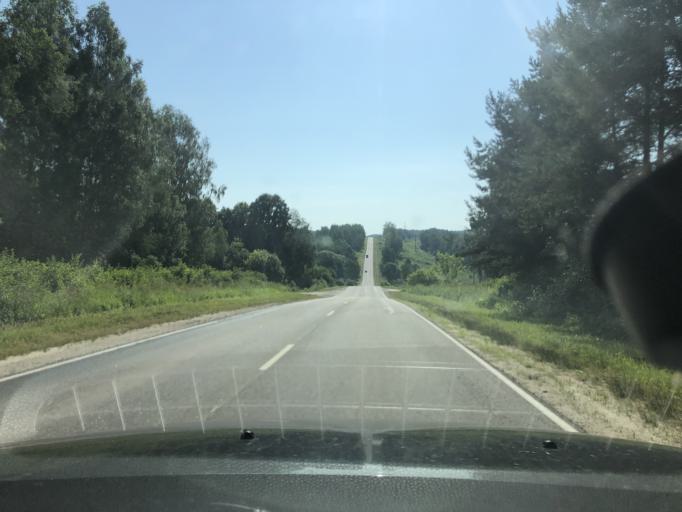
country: RU
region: Tula
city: Dubna
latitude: 54.1458
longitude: 36.9831
